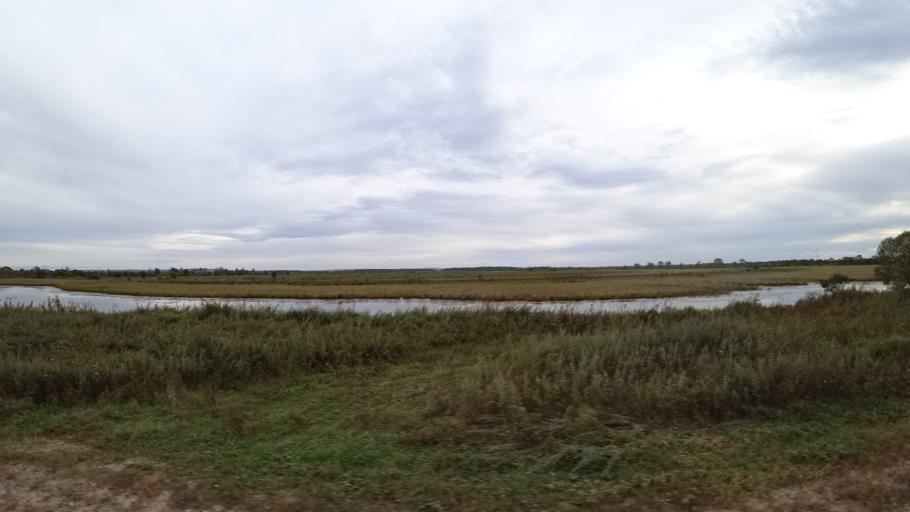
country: RU
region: Amur
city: Arkhara
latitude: 49.4305
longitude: 130.2384
